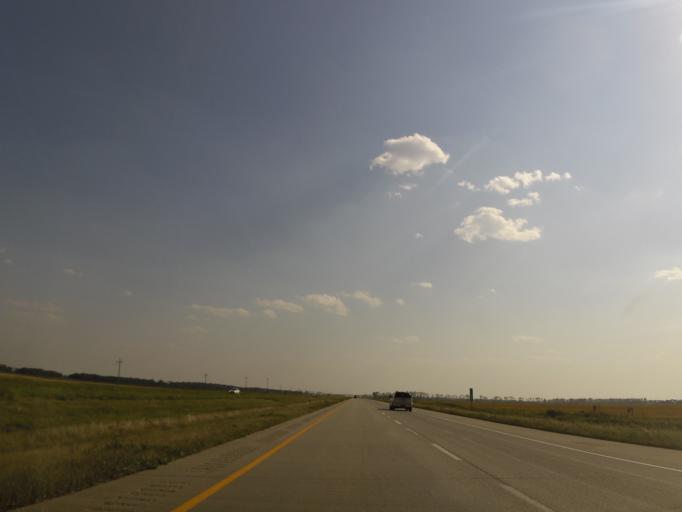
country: US
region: North Dakota
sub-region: Walsh County
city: Grafton
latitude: 48.2564
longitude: -97.1891
